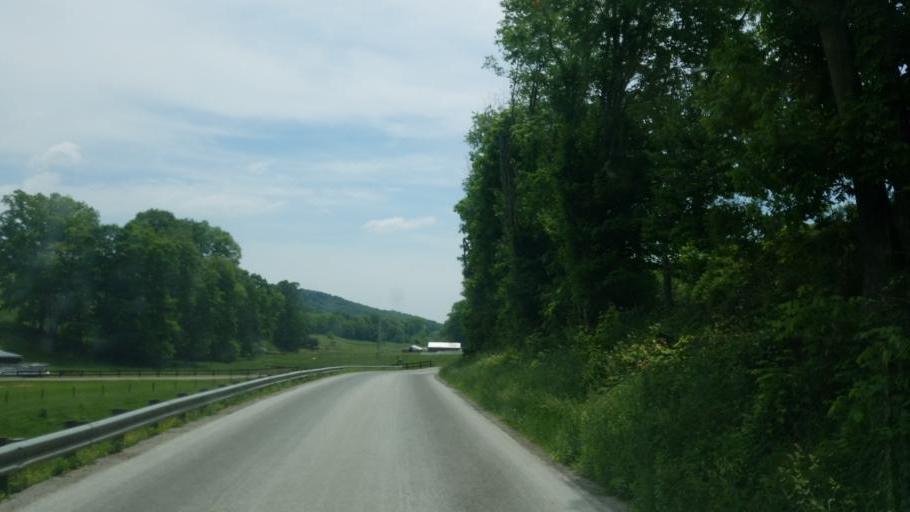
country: US
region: Ohio
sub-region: Coshocton County
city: West Lafayette
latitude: 40.4137
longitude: -81.7730
